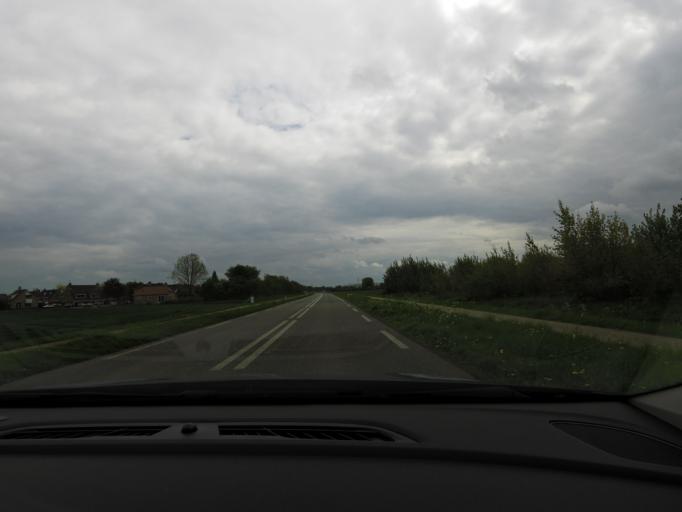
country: NL
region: Gelderland
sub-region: Gemeente Tiel
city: Tiel
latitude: 51.8990
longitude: 5.3730
